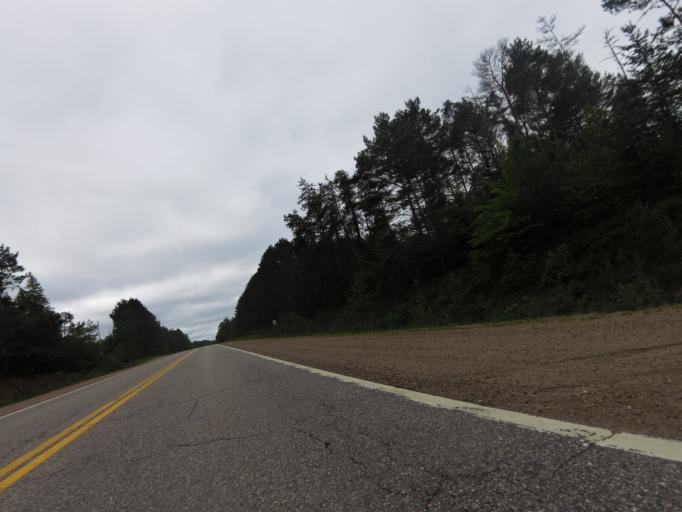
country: CA
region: Quebec
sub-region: Outaouais
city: Shawville
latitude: 45.8701
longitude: -76.4052
